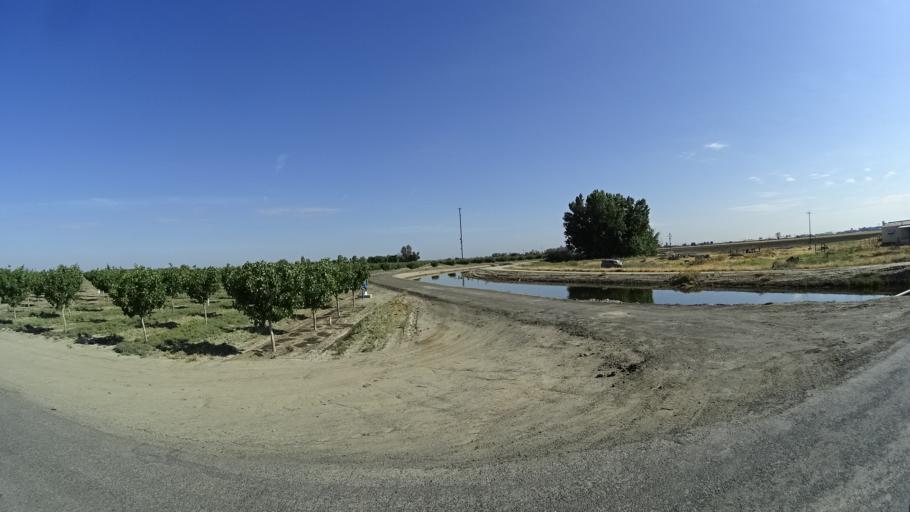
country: US
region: California
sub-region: Kings County
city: Stratford
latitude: 36.2259
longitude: -119.7891
